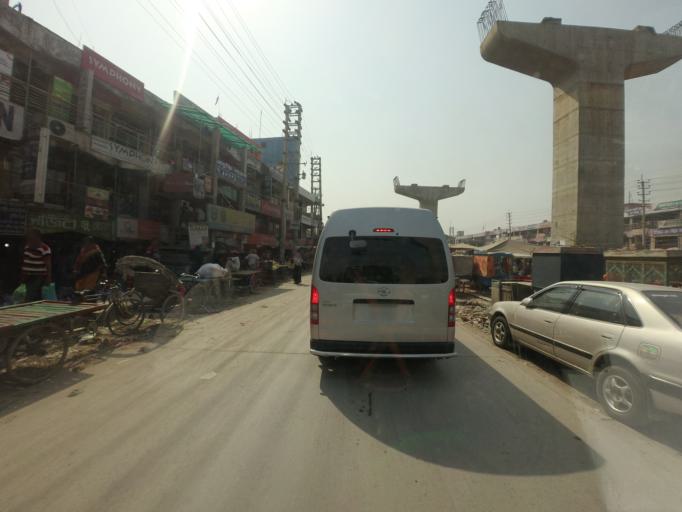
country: BD
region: Dhaka
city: Paltan
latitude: 23.7849
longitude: 90.5666
